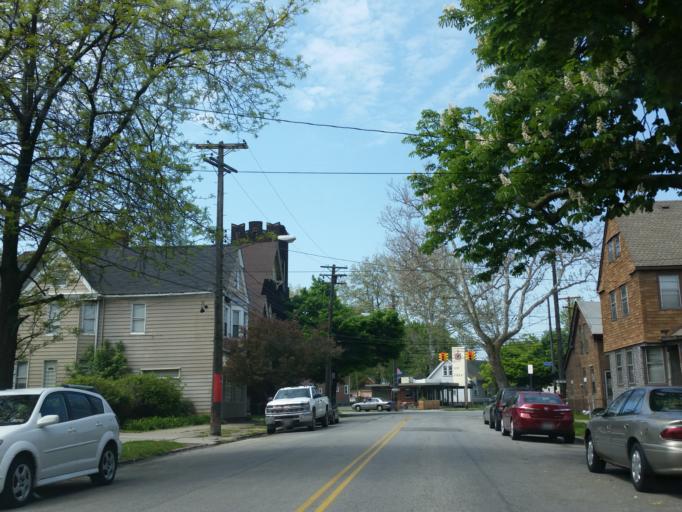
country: US
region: Ohio
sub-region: Cuyahoga County
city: Cleveland
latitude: 41.4810
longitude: -81.7157
